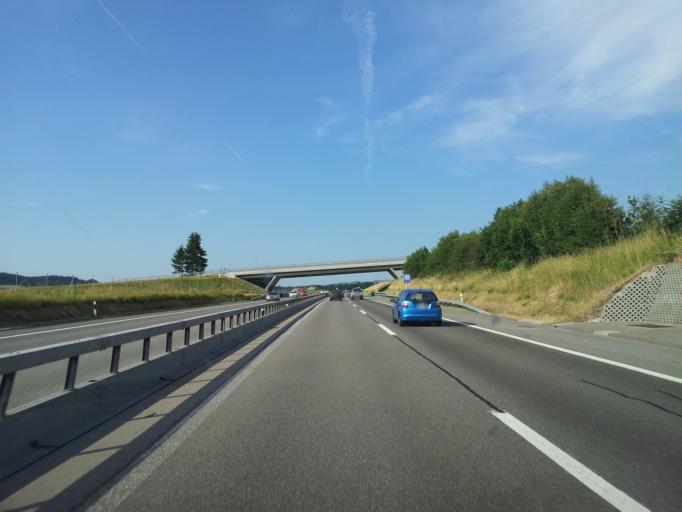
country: CH
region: Fribourg
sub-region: Veveyse District
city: Chatel-Saint-Denis
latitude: 46.5845
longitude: 6.9279
